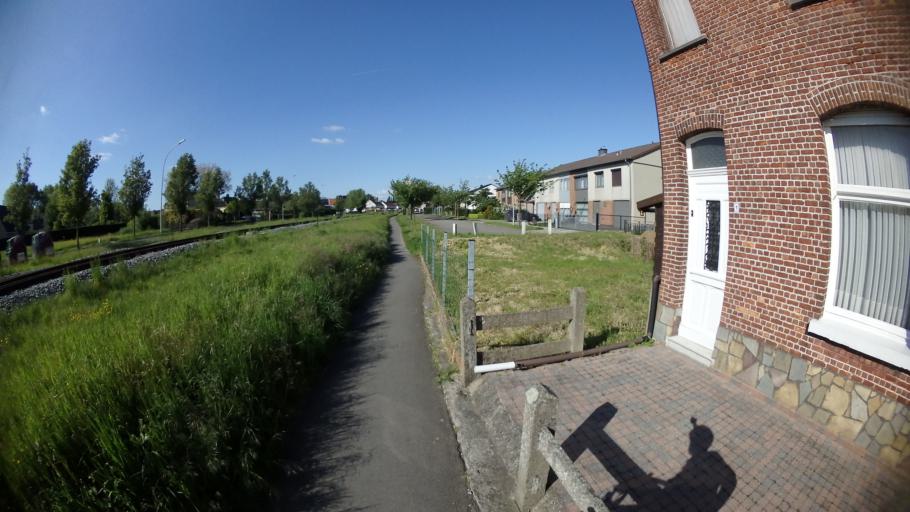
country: BE
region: Flanders
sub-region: Provincie Antwerpen
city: Sint-Amands
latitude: 51.0534
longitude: 4.2082
